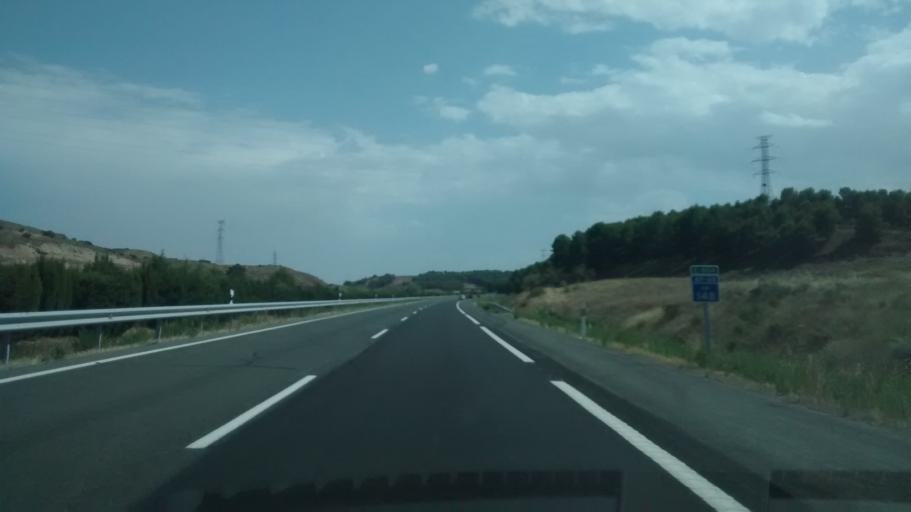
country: ES
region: La Rioja
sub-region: Provincia de La Rioja
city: Arrubal
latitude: 42.4065
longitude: -2.2535
